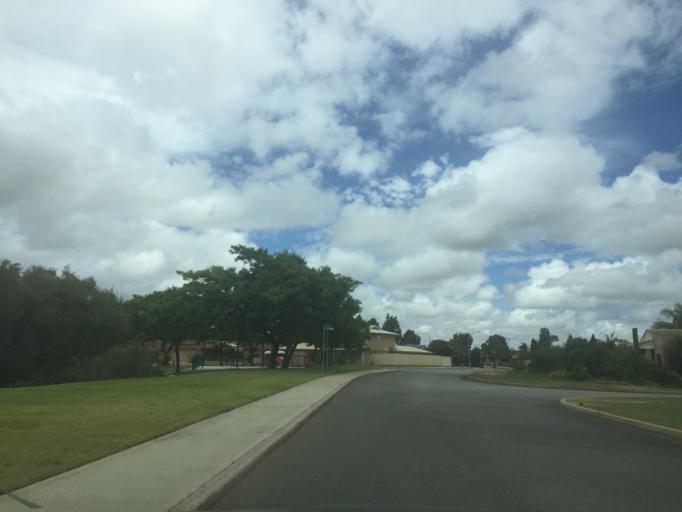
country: AU
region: Western Australia
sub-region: Gosnells
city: Thornlie
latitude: -32.0749
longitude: 115.9591
